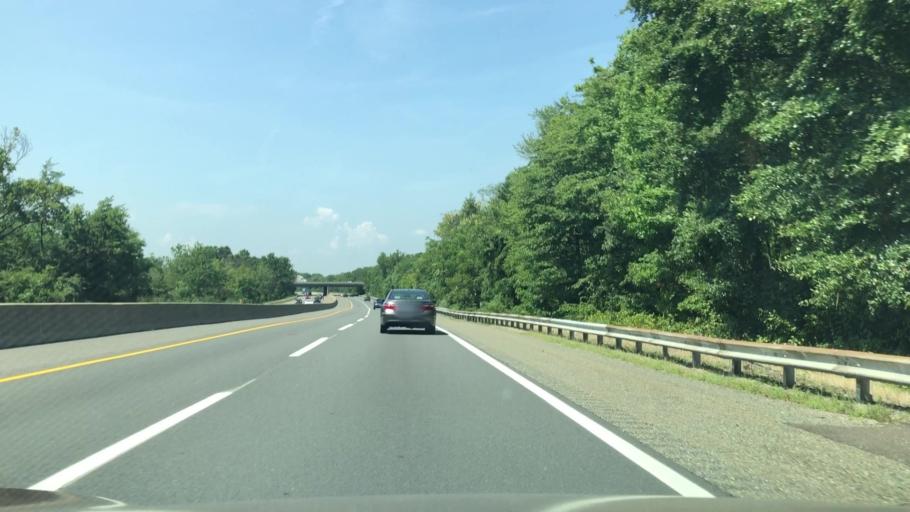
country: US
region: New Jersey
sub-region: Camden County
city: Bellmawr
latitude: 39.8565
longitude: -75.0931
